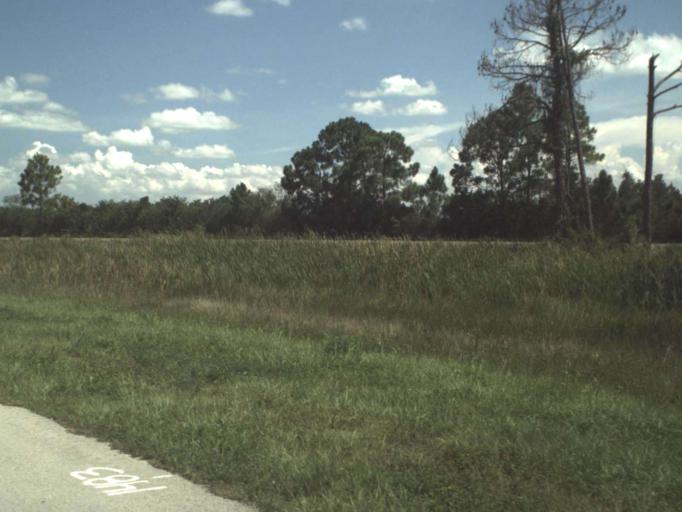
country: US
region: Florida
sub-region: Palm Beach County
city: Limestone Creek
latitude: 26.9214
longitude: -80.3194
